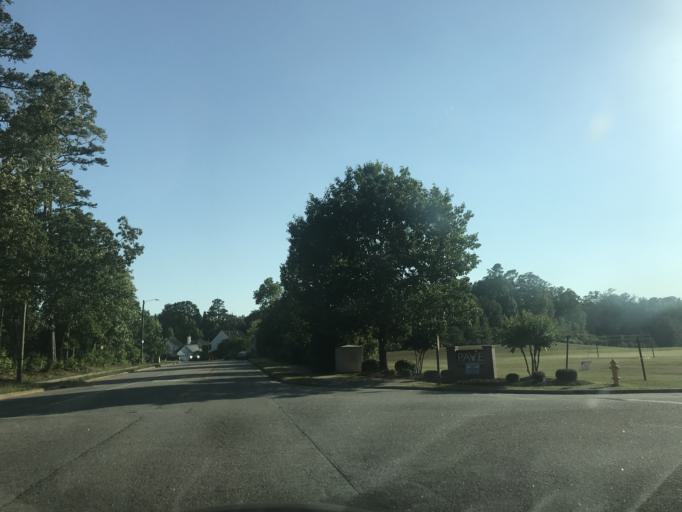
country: US
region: North Carolina
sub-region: Wake County
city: Garner
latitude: 35.7364
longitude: -78.6167
